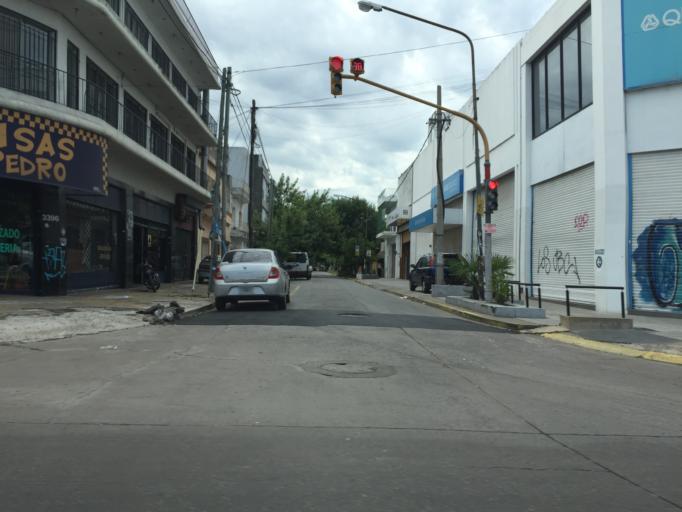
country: AR
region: Buenos Aires
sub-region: Partido de Lanus
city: Lanus
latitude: -34.6950
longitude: -58.3906
